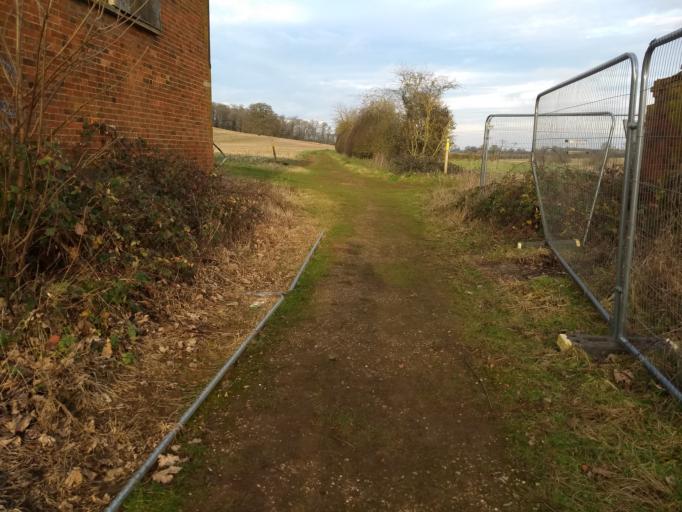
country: GB
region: England
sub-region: Central Bedfordshire
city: Woburn
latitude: 51.9915
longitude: -0.6355
